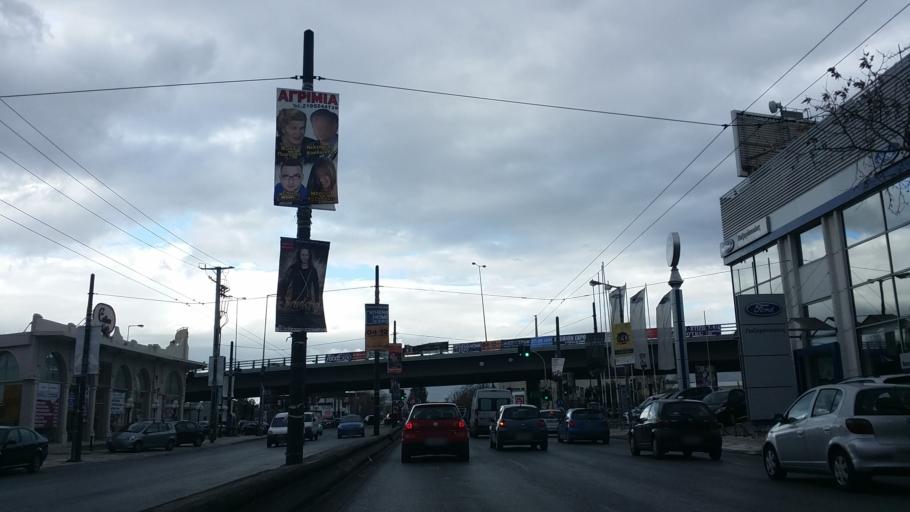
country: GR
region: Attica
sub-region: Nomarchia Athinas
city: Aigaleo
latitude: 37.9763
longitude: 23.6757
